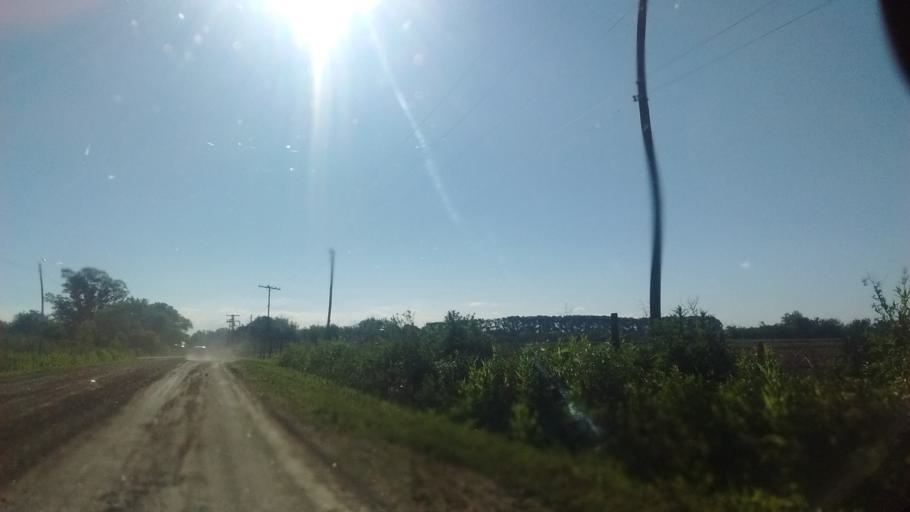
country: AR
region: Santa Fe
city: Funes
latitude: -32.8609
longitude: -60.8011
